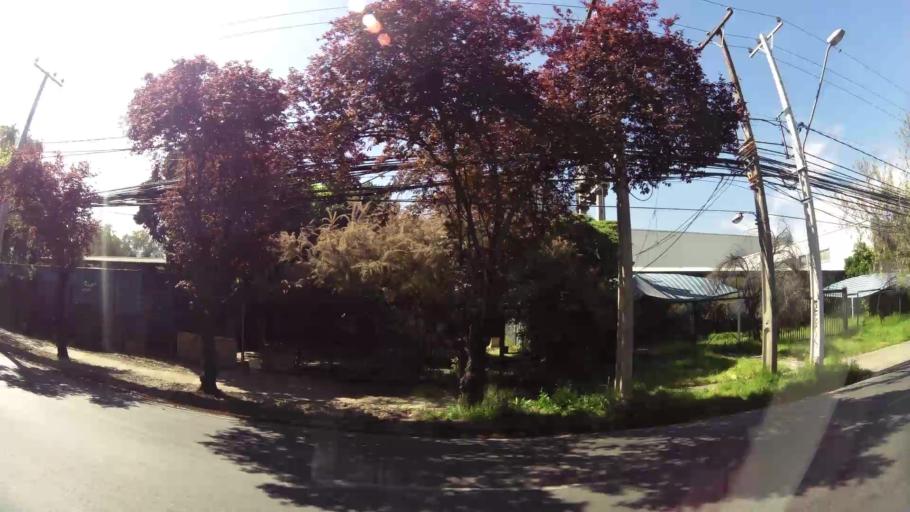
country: CL
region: Santiago Metropolitan
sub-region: Provincia de Santiago
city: Villa Presidente Frei, Nunoa, Santiago, Chile
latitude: -33.4548
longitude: -70.5445
